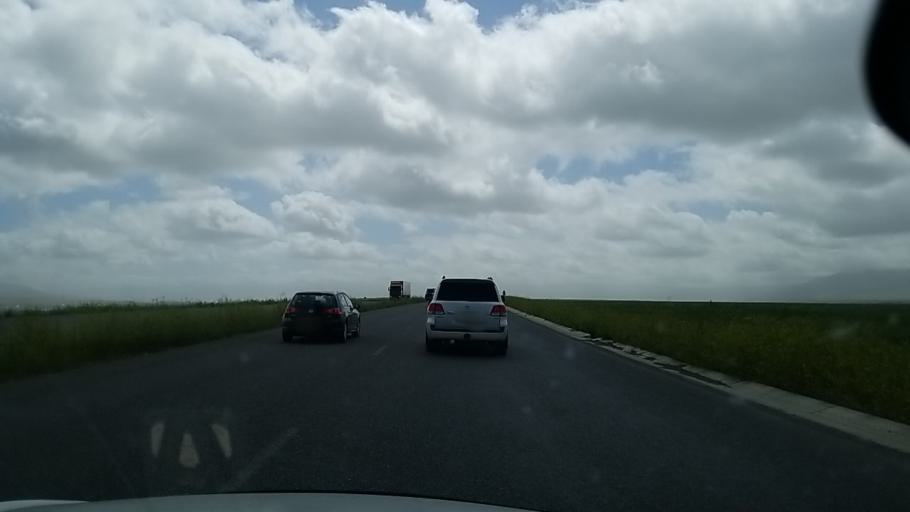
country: KZ
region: Ongtustik Qazaqstan
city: Kokterek
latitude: 42.5457
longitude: 70.2722
